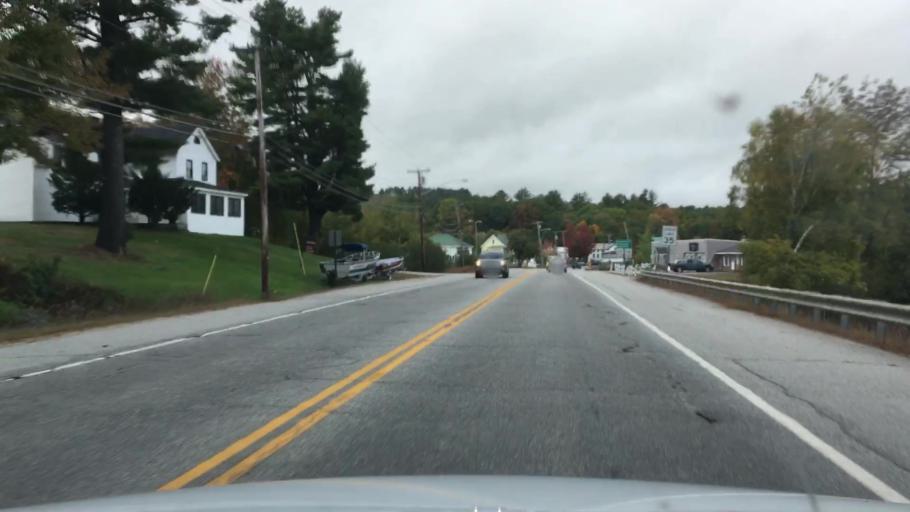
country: US
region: Maine
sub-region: Oxford County
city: Norway
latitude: 44.2128
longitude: -70.5736
